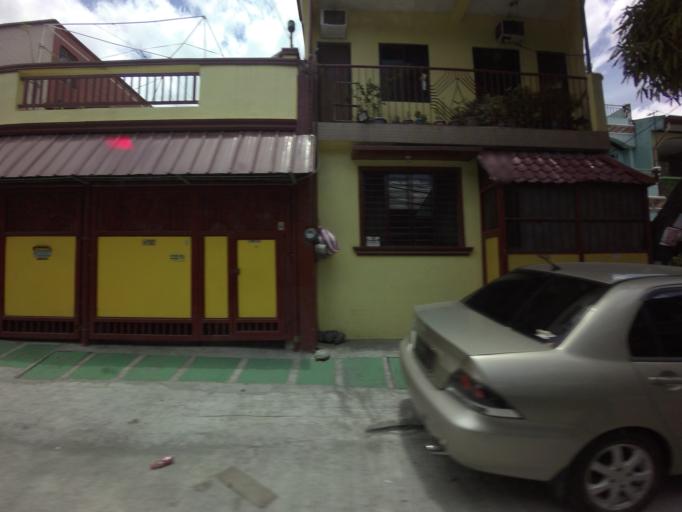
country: PH
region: Metro Manila
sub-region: Marikina
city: Calumpang
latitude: 14.6081
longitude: 121.1032
